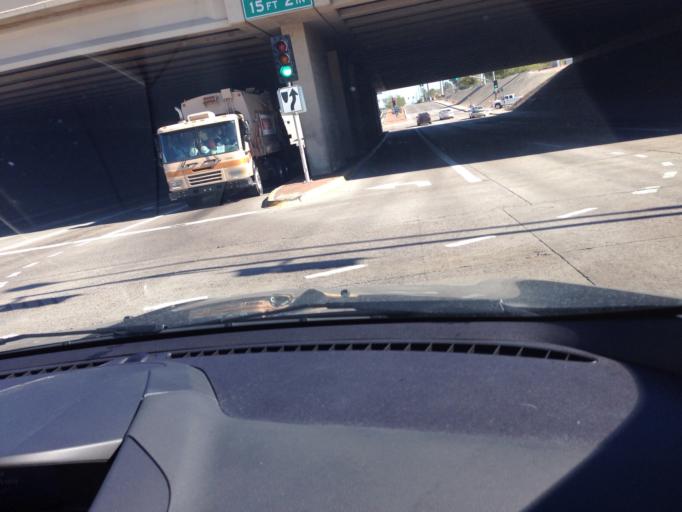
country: US
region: Arizona
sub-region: Maricopa County
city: Glendale
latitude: 33.6546
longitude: -112.1152
